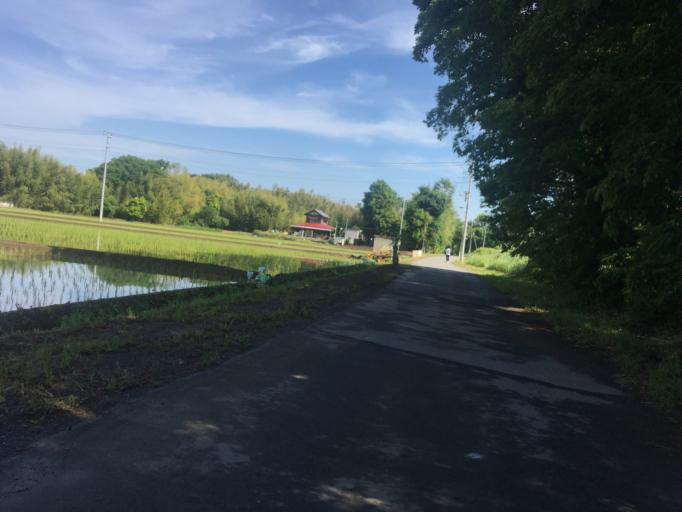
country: JP
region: Saitama
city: Shiki
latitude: 35.8600
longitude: 139.5935
